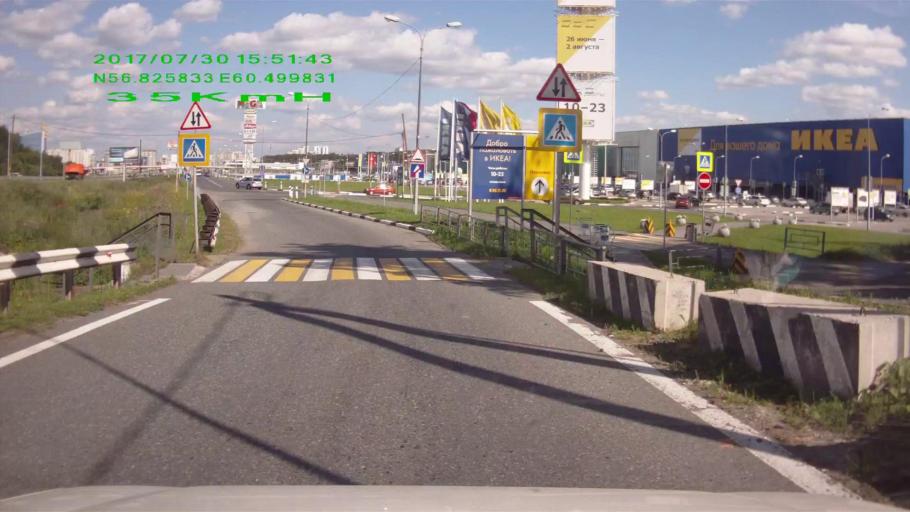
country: RU
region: Sverdlovsk
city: Shirokaya Rechka
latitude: 56.8258
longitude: 60.4999
